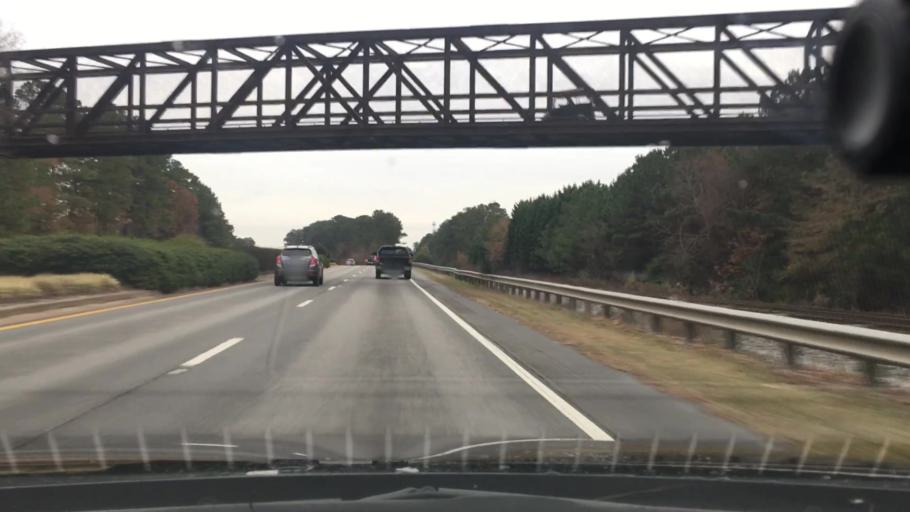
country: US
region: Georgia
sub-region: Fayette County
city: Peachtree City
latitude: 33.4053
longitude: -84.6000
